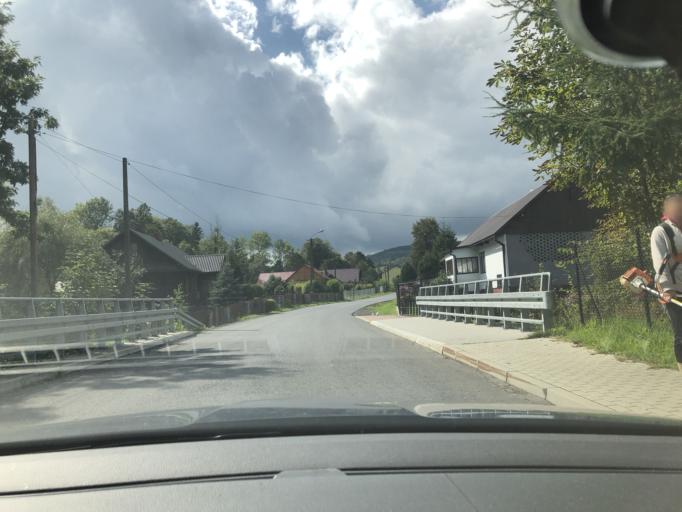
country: PL
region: Lesser Poland Voivodeship
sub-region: Powiat suski
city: Lachowice
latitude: 49.7079
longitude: 19.4270
